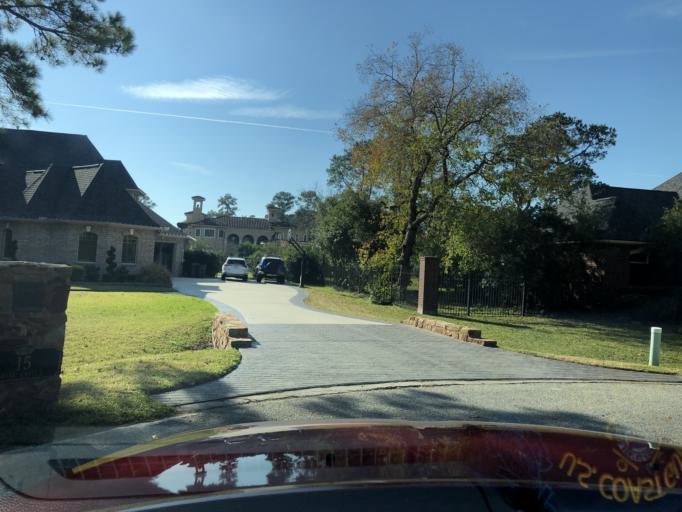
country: US
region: Texas
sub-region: Harris County
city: Tomball
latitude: 30.0411
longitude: -95.5595
